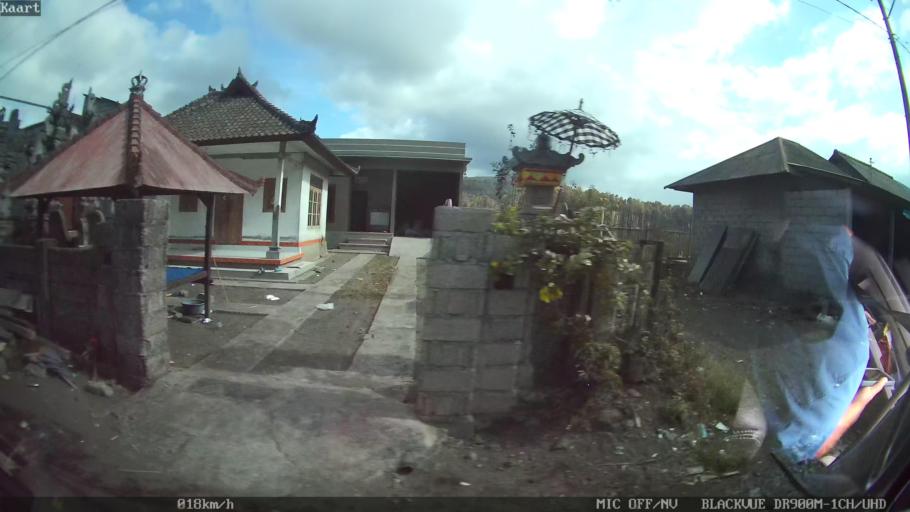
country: ID
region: Bali
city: Banjar Trunyan
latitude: -8.2153
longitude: 115.3753
